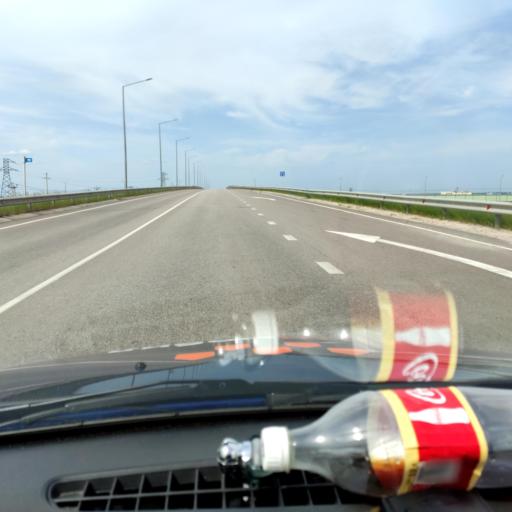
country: RU
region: Voronezj
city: Novaya Usman'
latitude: 51.5882
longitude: 39.3742
